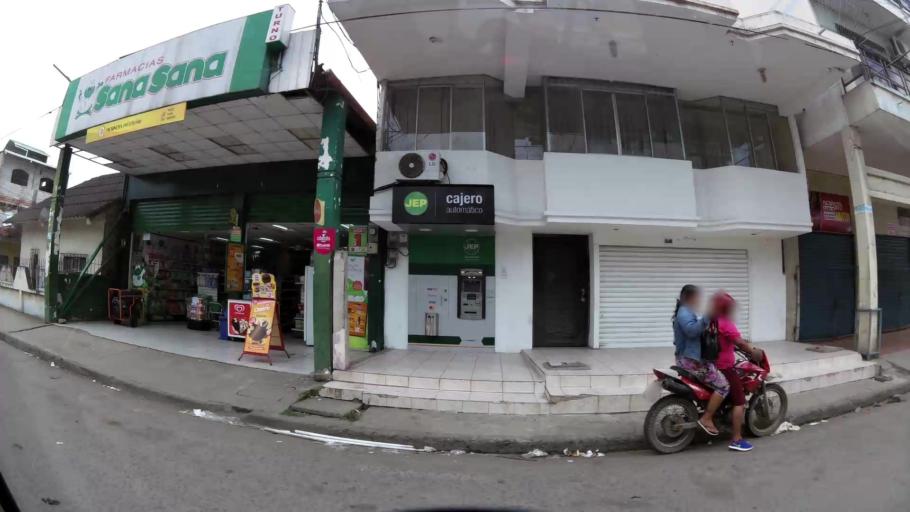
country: EC
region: El Oro
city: Machala
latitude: -3.2591
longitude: -79.9501
